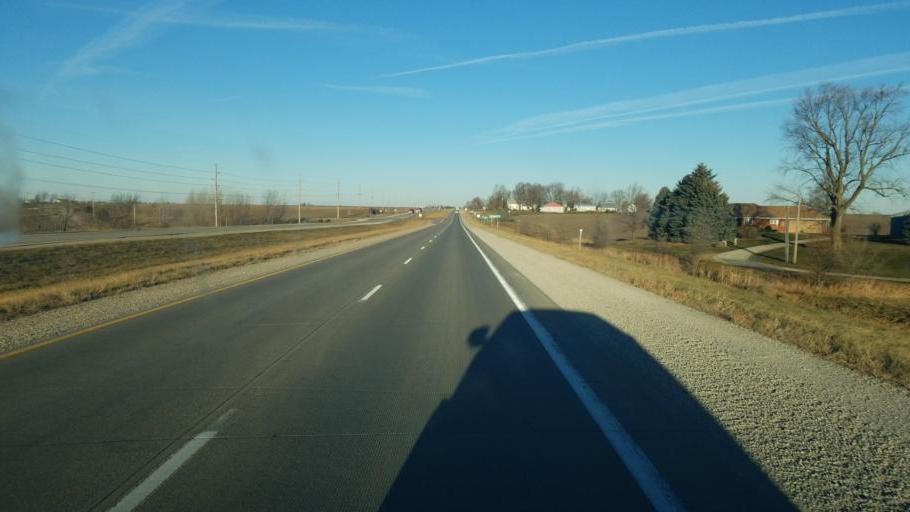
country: US
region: Iowa
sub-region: Mahaska County
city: Oskaloosa
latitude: 41.3349
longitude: -92.7268
